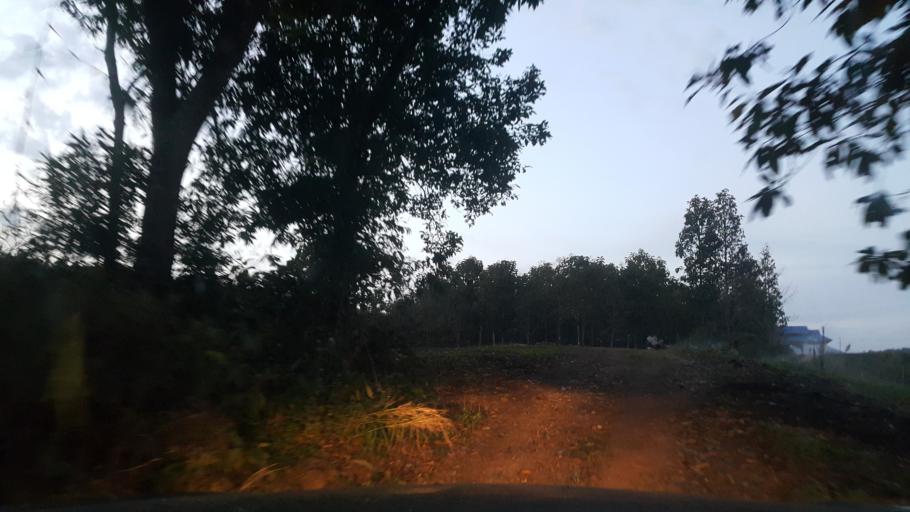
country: TH
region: Chiang Mai
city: Samoeng
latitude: 18.9513
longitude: 98.6724
